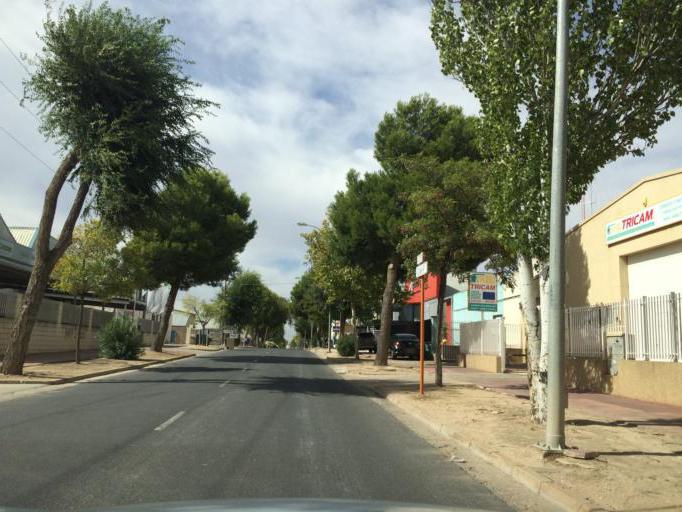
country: ES
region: Castille-La Mancha
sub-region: Provincia de Albacete
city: Albacete
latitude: 39.0117
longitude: -1.8880
